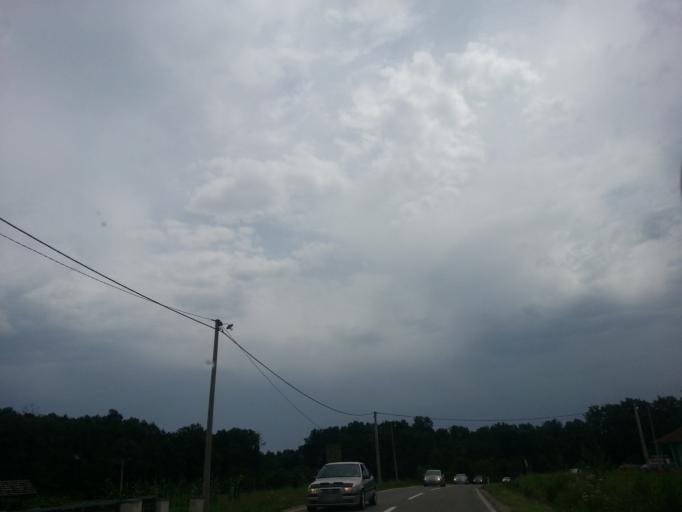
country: BA
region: Republika Srpska
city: Velika Obarska
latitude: 44.7995
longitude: 19.0830
